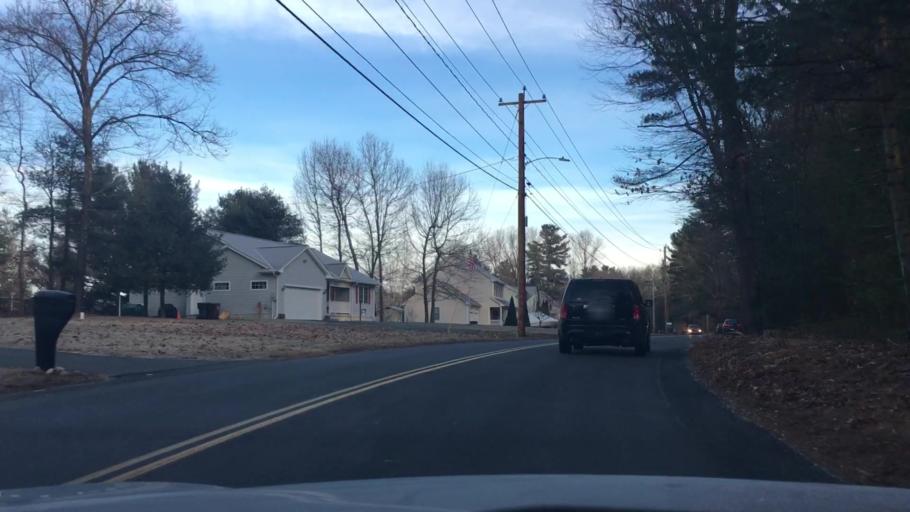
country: US
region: Massachusetts
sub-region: Hampden County
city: Westfield
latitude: 42.1290
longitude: -72.7231
